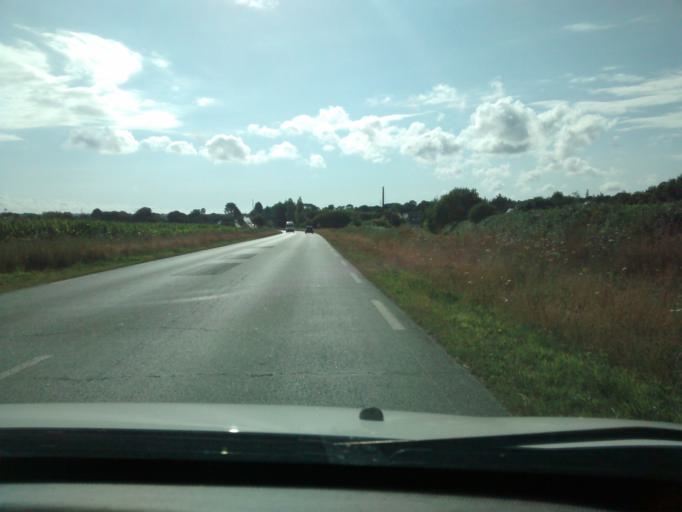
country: FR
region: Brittany
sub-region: Departement des Cotes-d'Armor
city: Rospez
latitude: 48.7439
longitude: -3.3951
